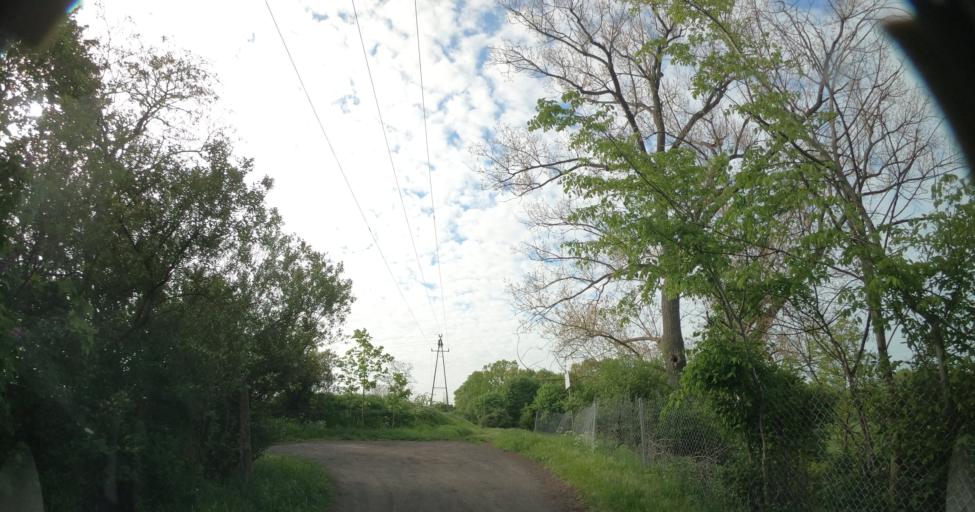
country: PL
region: West Pomeranian Voivodeship
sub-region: Powiat stargardzki
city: Stargard Szczecinski
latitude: 53.3439
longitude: 15.0621
